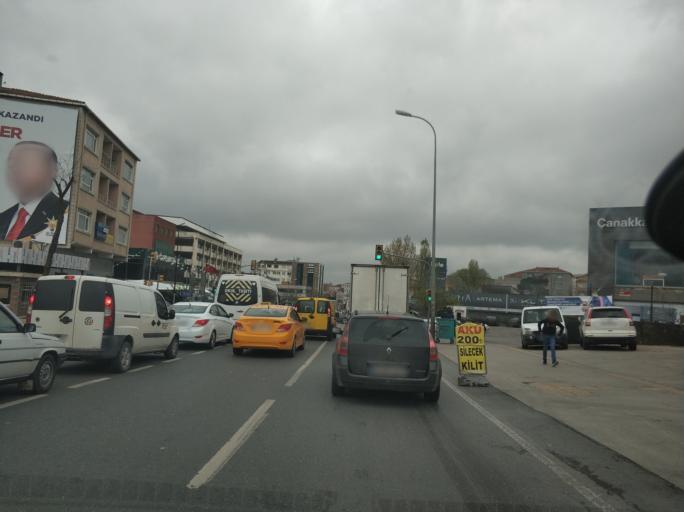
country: TR
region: Istanbul
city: Umraniye
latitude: 41.0192
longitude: 29.1312
